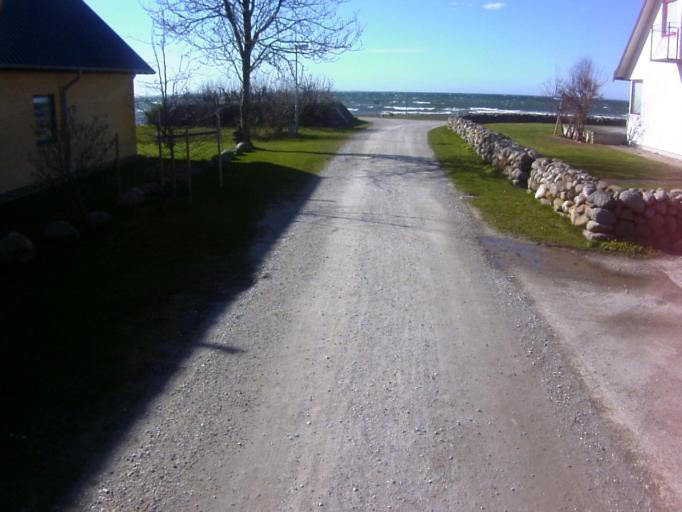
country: SE
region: Skane
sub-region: Kavlinge Kommun
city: Hofterup
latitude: 55.7600
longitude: 12.9079
